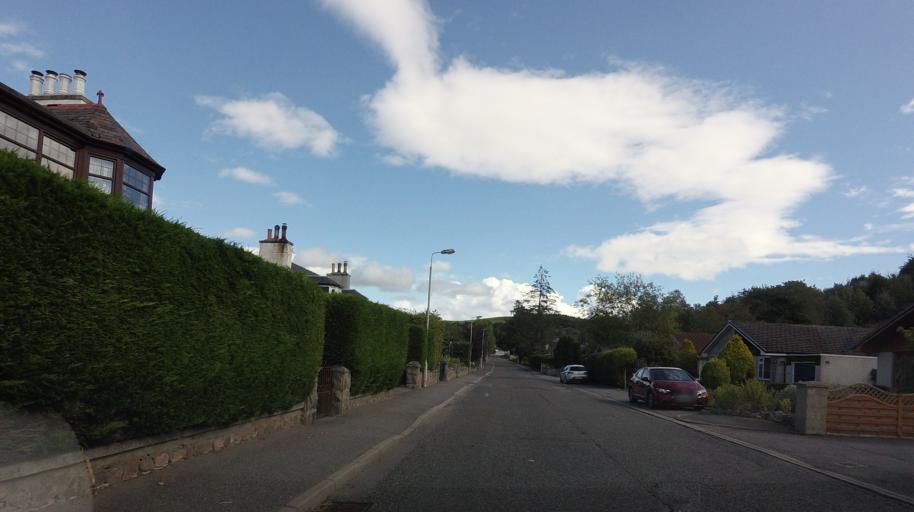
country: GB
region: Scotland
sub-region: Aberdeenshire
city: Torphins
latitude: 57.1266
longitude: -2.6876
